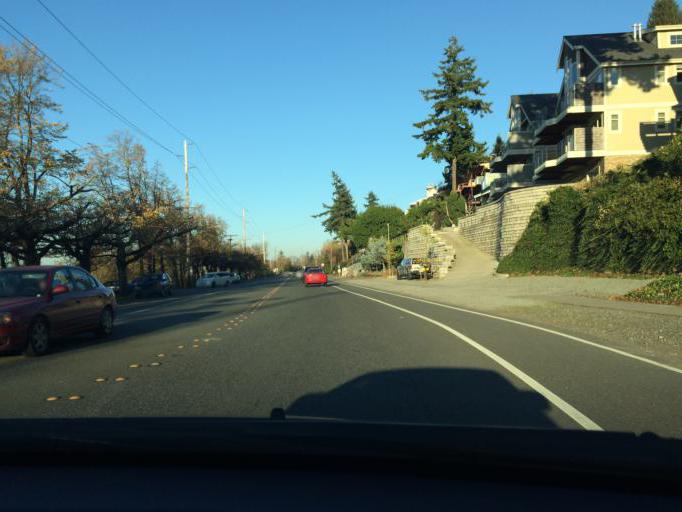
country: US
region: Washington
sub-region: Whatcom County
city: Bellingham
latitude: 48.7331
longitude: -122.4985
